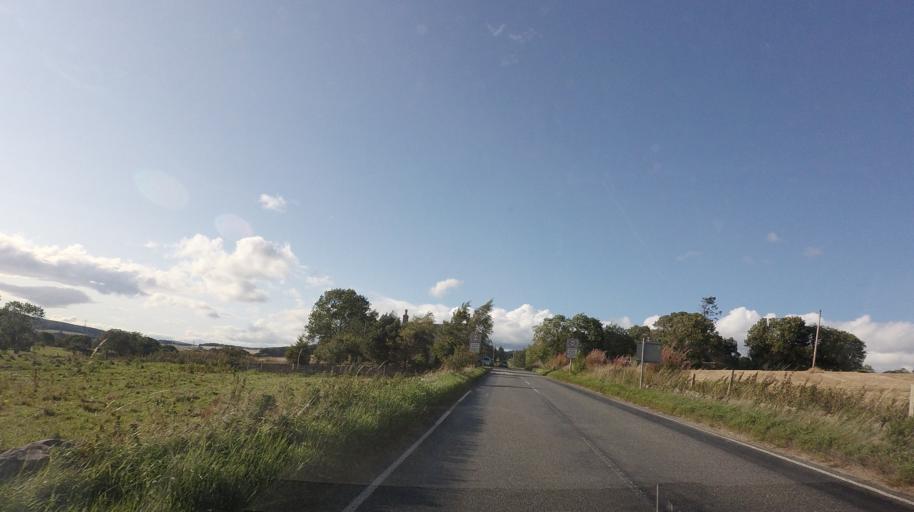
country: GB
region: Scotland
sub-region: Aberdeenshire
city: Kemnay
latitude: 57.1364
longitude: -2.4307
